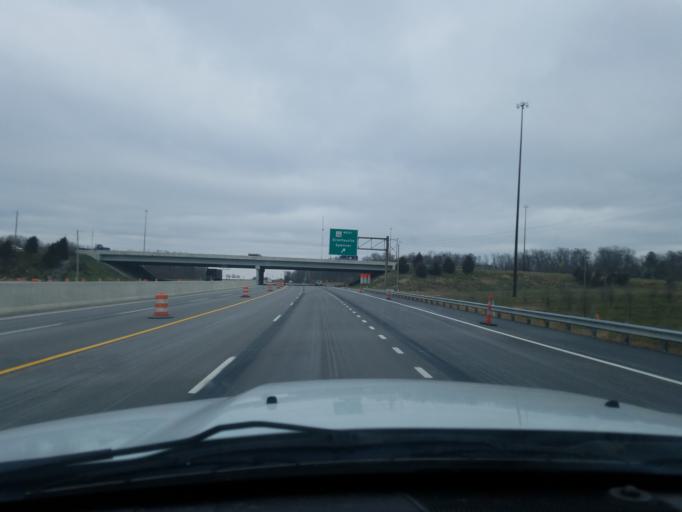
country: US
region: Indiana
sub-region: Monroe County
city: Bloomington
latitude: 39.1856
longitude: -86.5553
